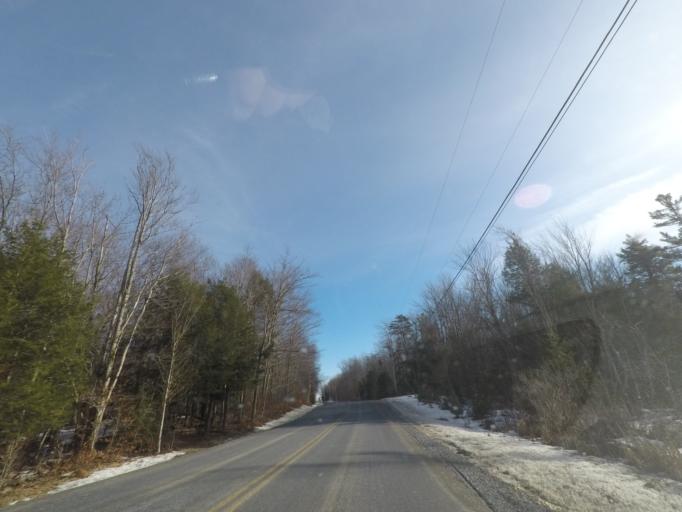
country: US
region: New York
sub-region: Rensselaer County
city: Poestenkill
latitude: 42.7505
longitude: -73.4164
